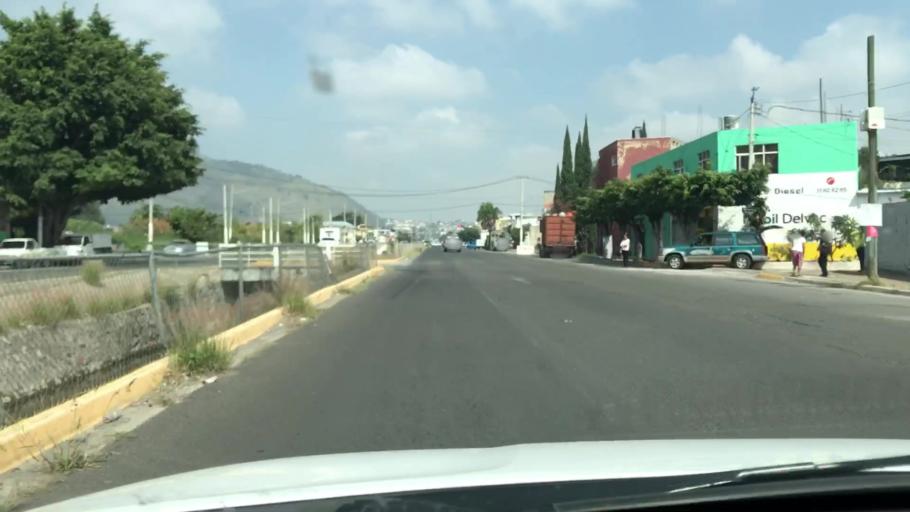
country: MX
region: Jalisco
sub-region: Tlajomulco de Zuniga
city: Palomar
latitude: 20.6378
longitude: -103.4464
